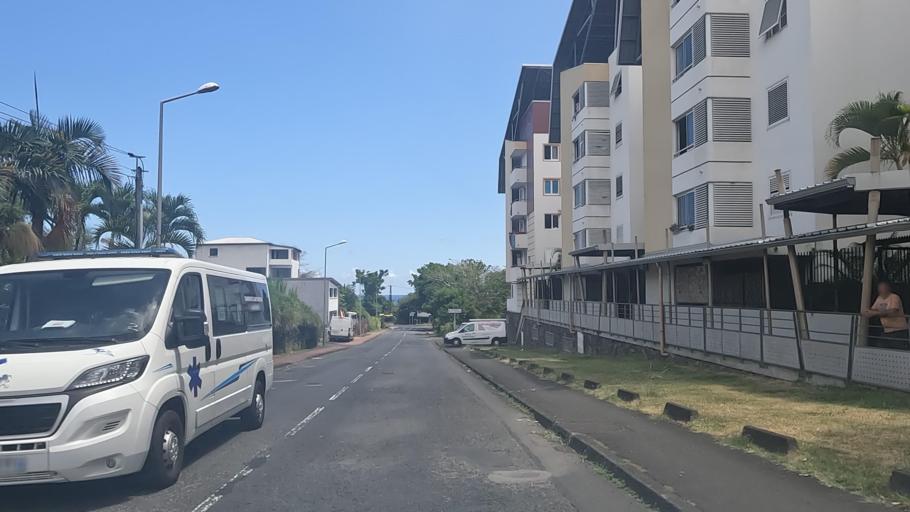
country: RE
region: Reunion
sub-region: Reunion
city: Saint-Benoit
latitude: -21.0318
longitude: 55.7088
